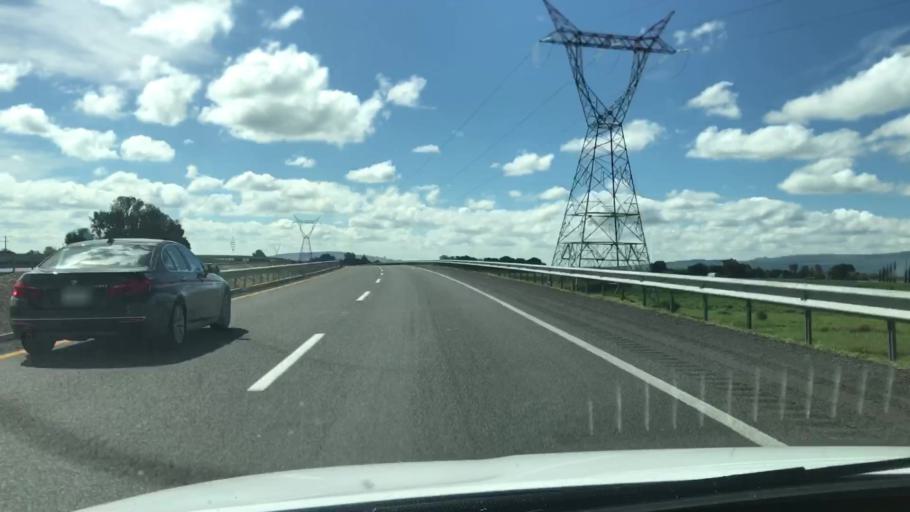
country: MX
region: Guanajuato
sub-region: Silao de la Victoria
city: La Aldea
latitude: 20.8863
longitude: -101.4832
